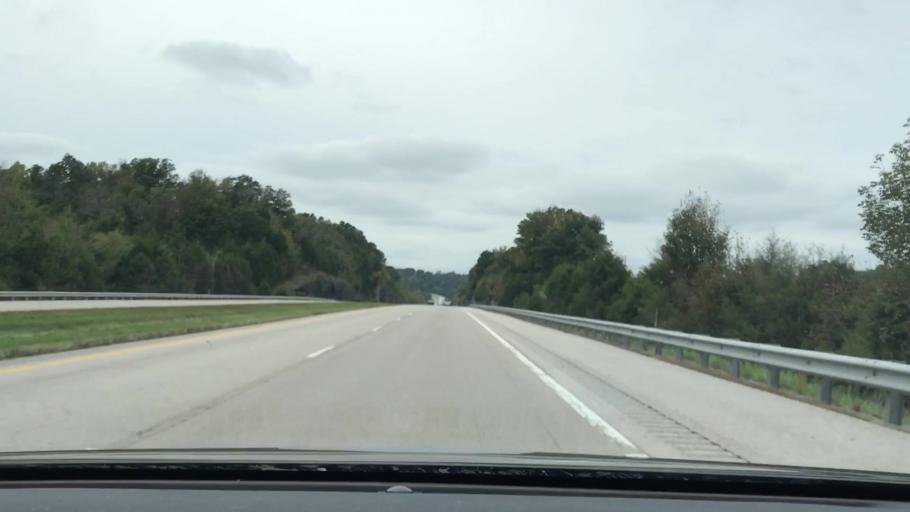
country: US
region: Kentucky
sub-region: Metcalfe County
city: Edmonton
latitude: 37.0288
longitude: -85.5273
